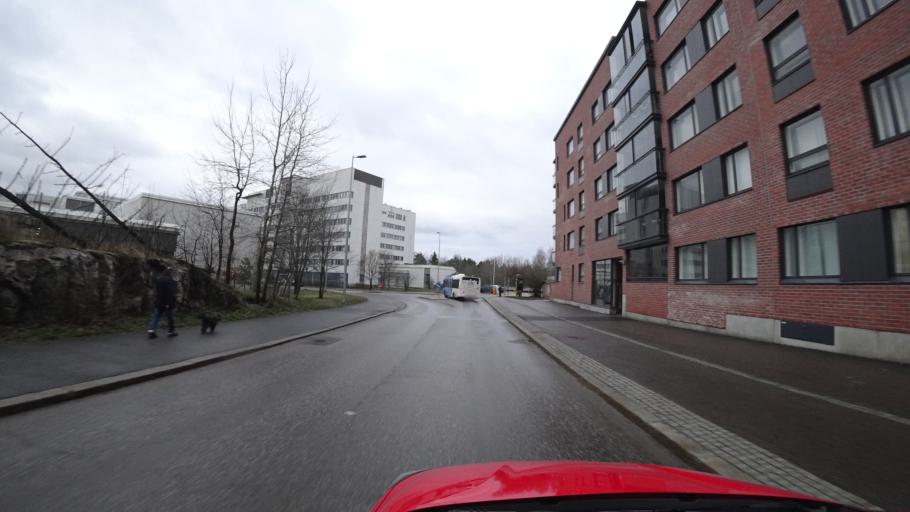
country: FI
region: Uusimaa
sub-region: Helsinki
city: Helsinki
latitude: 60.2047
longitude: 24.9184
